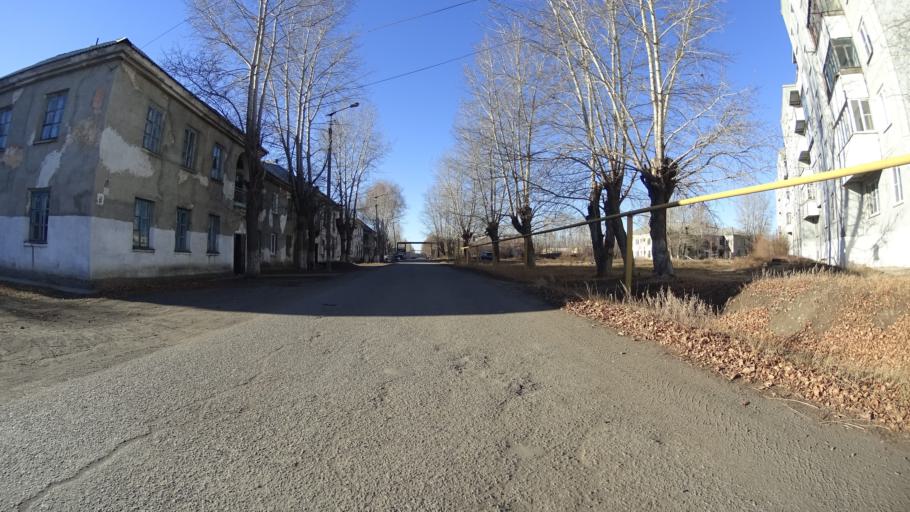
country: RU
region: Chelyabinsk
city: Troitsk
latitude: 54.1076
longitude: 61.5556
